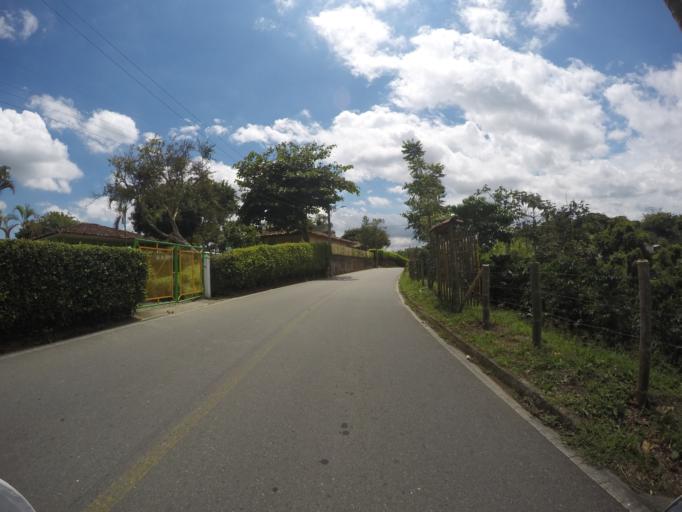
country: CO
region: Quindio
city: Quimbaya
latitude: 4.6266
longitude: -75.7452
